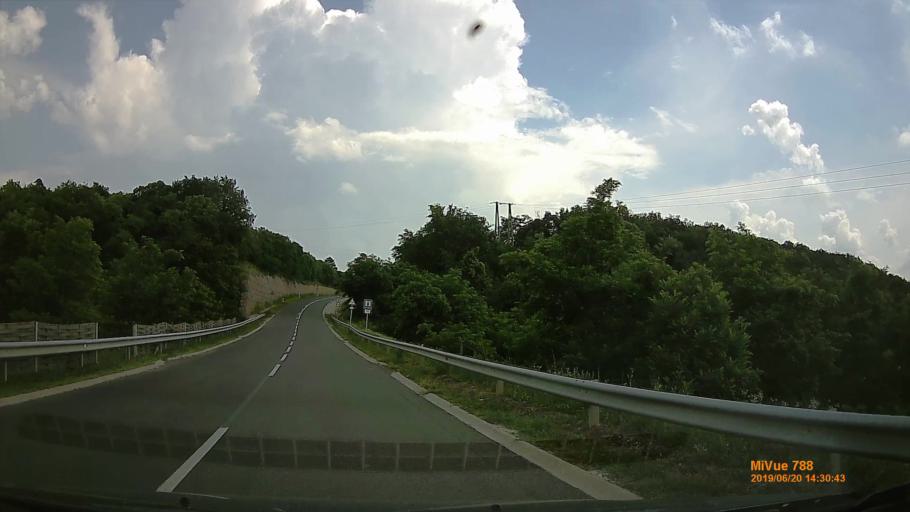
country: HU
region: Baranya
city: Hosszuheteny
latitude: 46.1461
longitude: 18.3470
